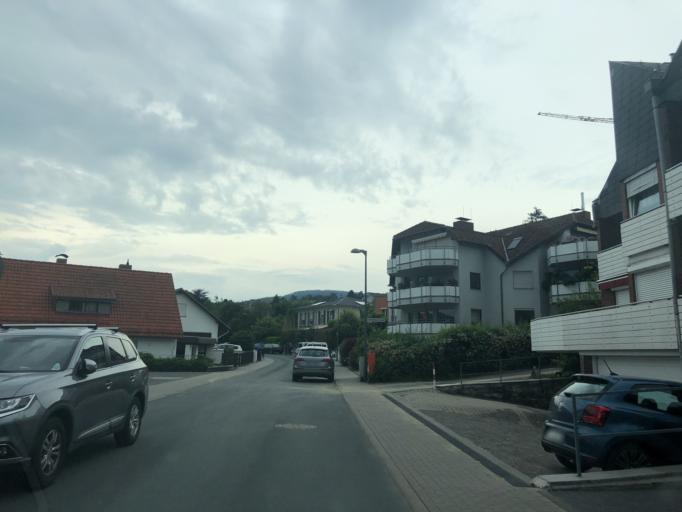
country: DE
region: Hesse
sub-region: Regierungsbezirk Darmstadt
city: Konigstein im Taunus
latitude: 50.1750
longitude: 8.4674
